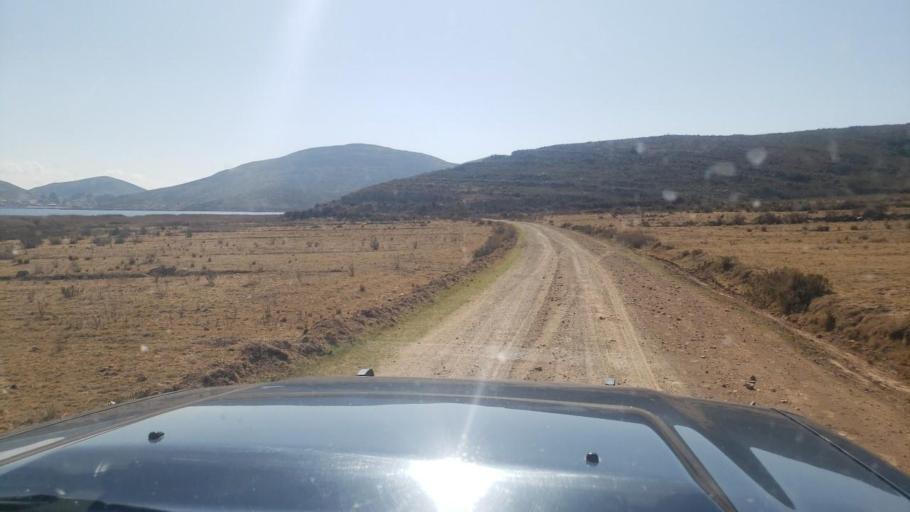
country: BO
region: La Paz
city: Huatajata
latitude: -16.3361
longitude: -68.6895
